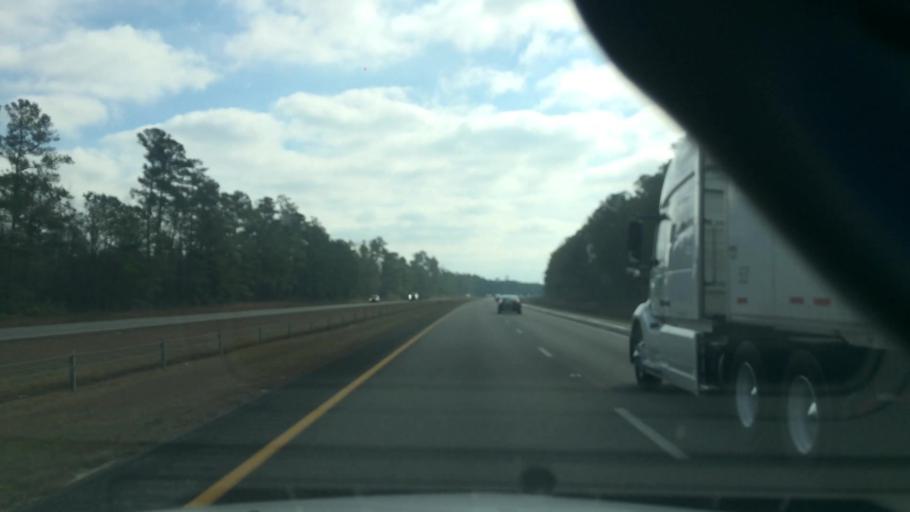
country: US
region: North Carolina
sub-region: Pender County
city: Burgaw
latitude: 34.5567
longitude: -77.8948
